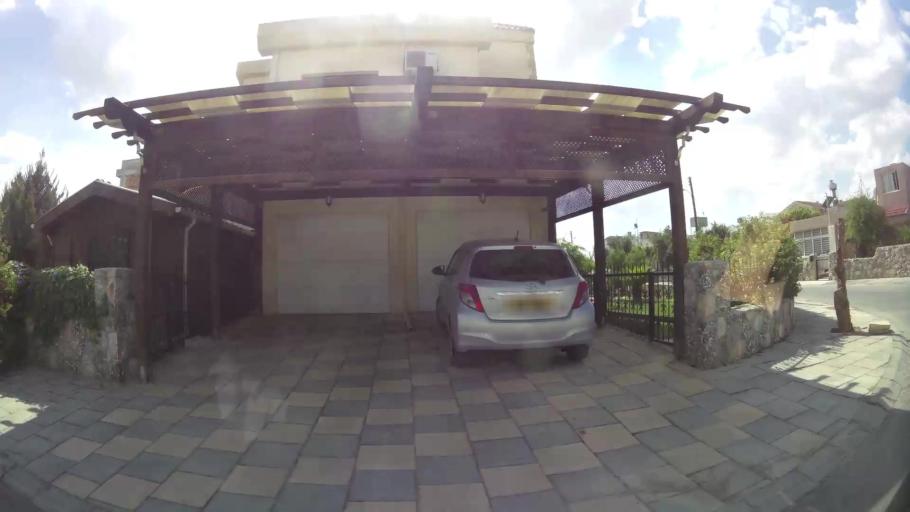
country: CY
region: Lefkosia
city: Nicosia
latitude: 35.2168
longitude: 33.2966
